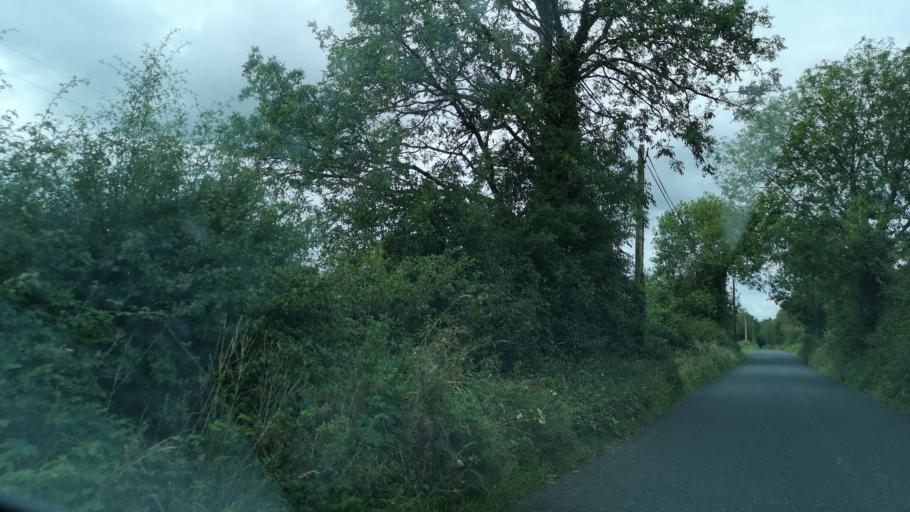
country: IE
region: Connaught
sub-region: County Galway
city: Loughrea
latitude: 53.1593
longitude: -8.4577
